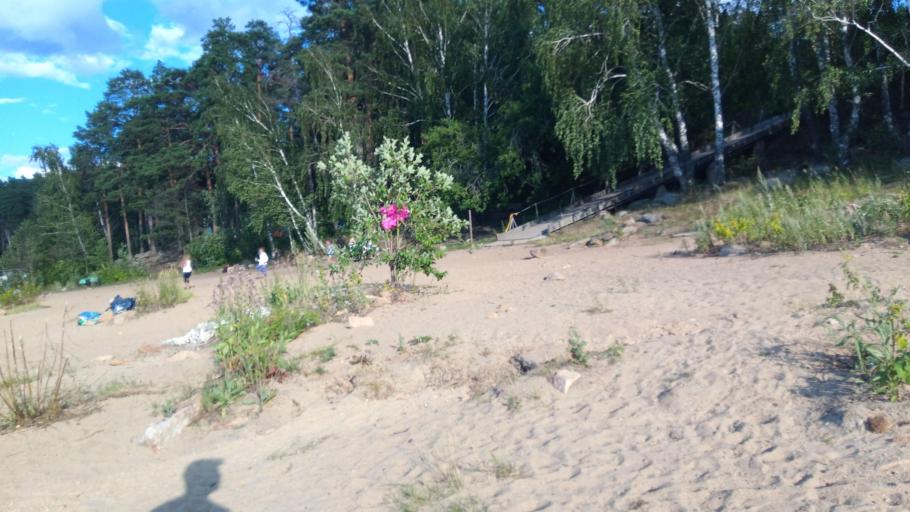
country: RU
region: Chelyabinsk
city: Chebarkul'
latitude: 55.0219
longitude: 60.3129
